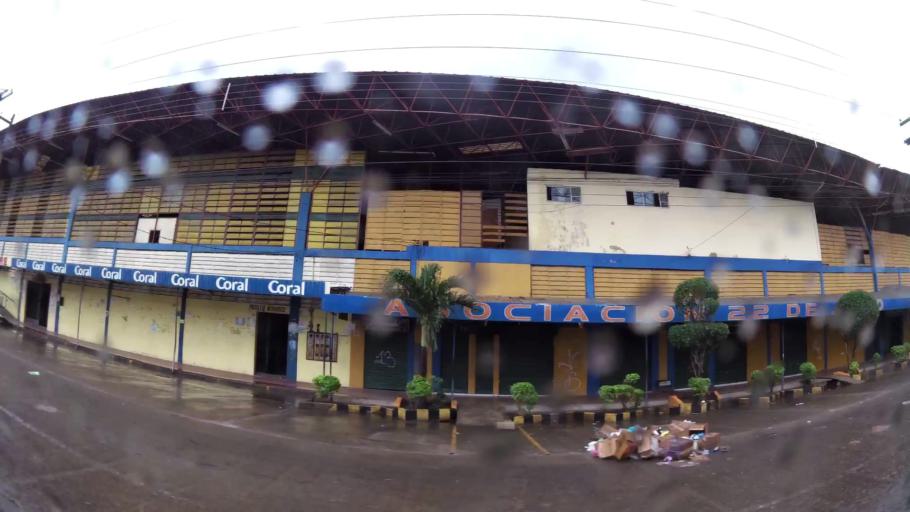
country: BO
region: Santa Cruz
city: Santa Cruz de la Sierra
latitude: -17.7911
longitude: -63.1537
